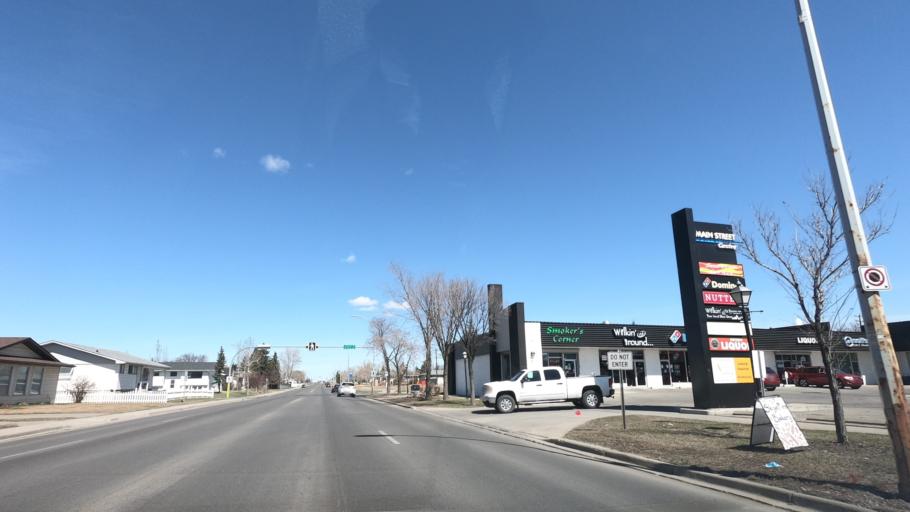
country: CA
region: Alberta
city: Airdrie
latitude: 51.2947
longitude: -114.0134
